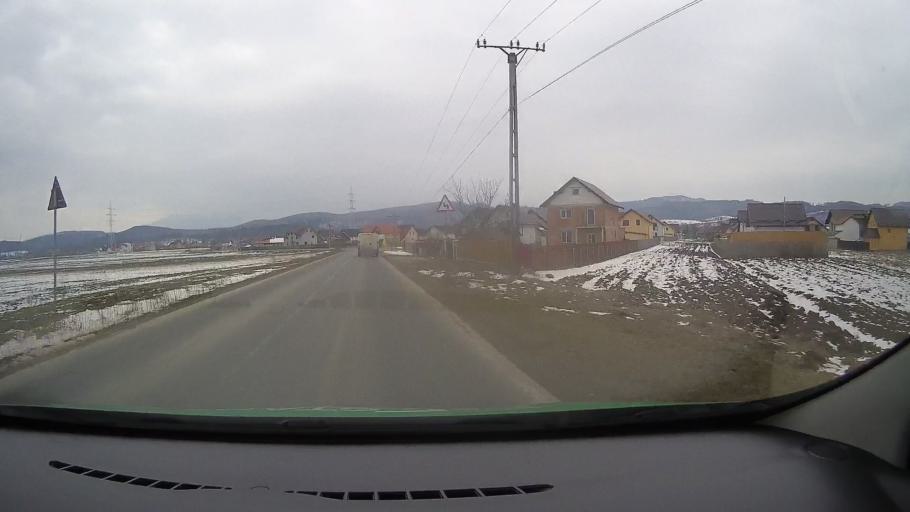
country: RO
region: Brasov
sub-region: Comuna Vulcan
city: Vulcan
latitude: 45.6365
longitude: 25.4321
